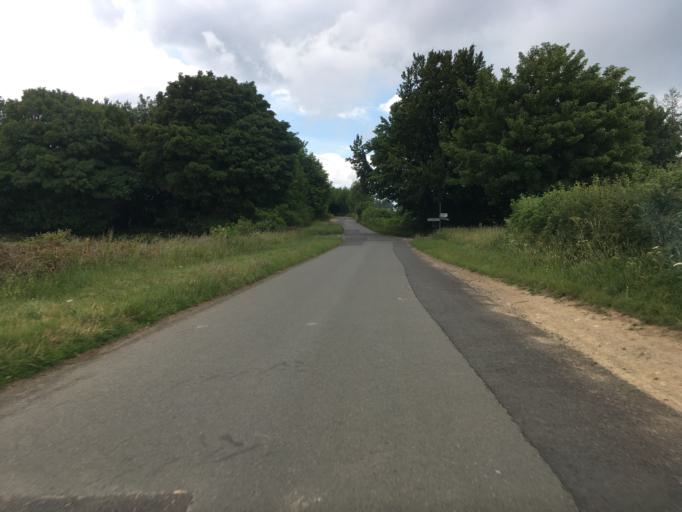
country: GB
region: England
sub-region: Gloucestershire
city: Coates
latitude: 51.7574
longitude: -2.0598
